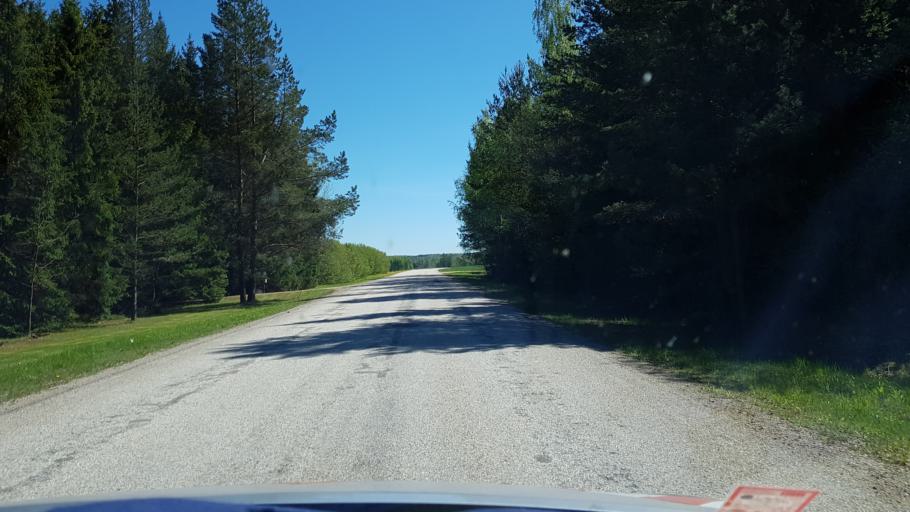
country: EE
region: Tartu
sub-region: UElenurme vald
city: Ulenurme
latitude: 58.2867
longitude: 26.8991
